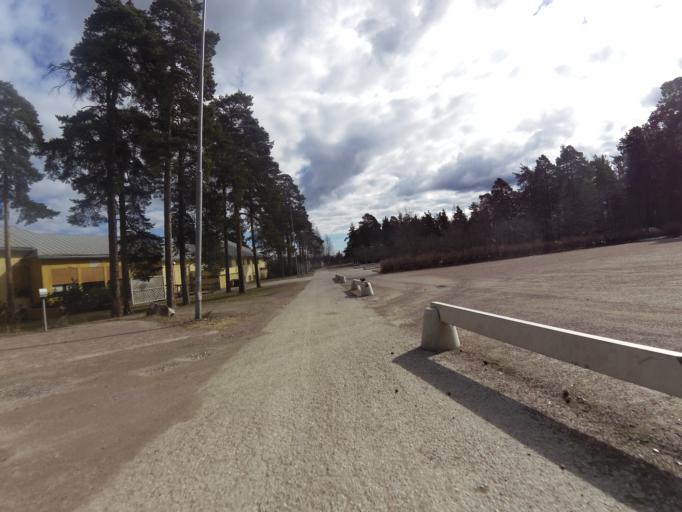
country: SE
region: Gaevleborg
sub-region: Gavle Kommun
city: Gavle
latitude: 60.6871
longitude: 17.1300
